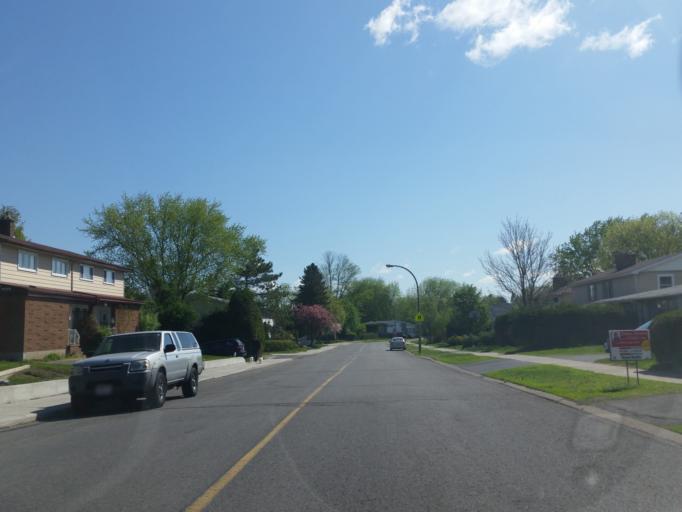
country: CA
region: Ontario
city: Ottawa
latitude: 45.3522
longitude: -75.7251
